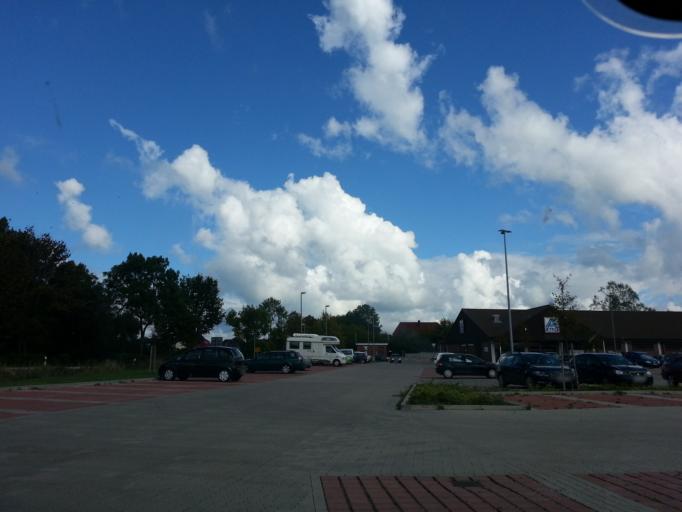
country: DE
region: Schleswig-Holstein
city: Heiligenhafen
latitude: 54.3636
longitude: 10.9658
